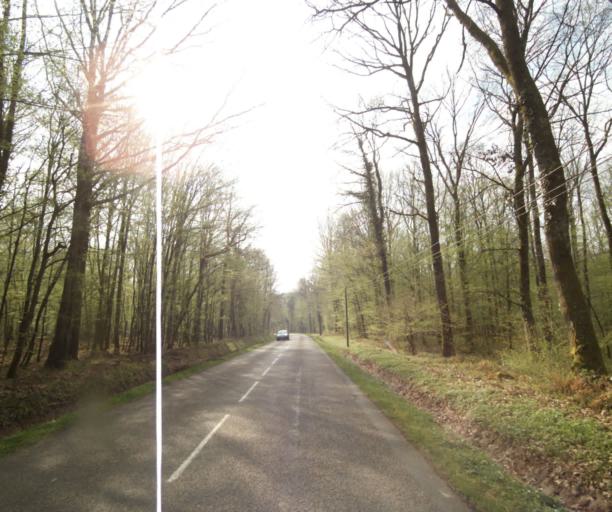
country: FR
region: Bourgogne
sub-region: Departement de Saone-et-Loire
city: Charolles
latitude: 46.4548
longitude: 4.2581
